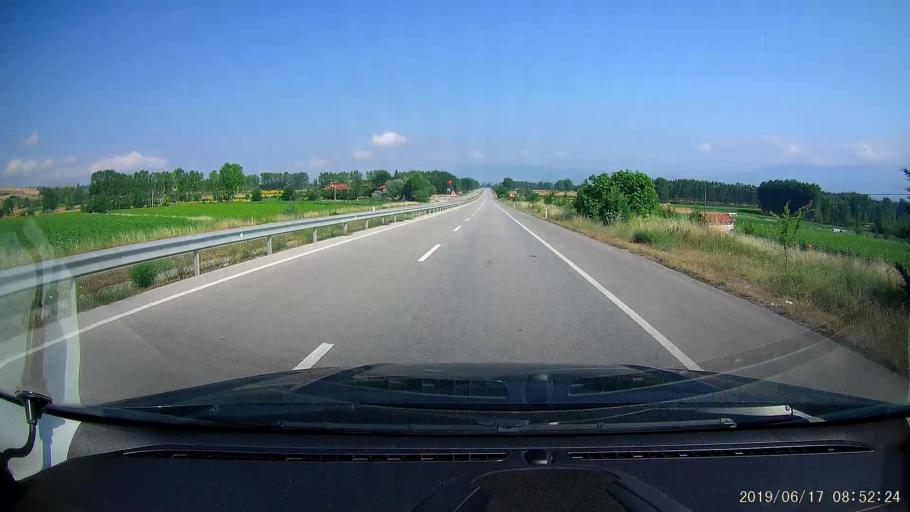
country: TR
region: Tokat
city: Erbaa
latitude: 40.6972
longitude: 36.4972
